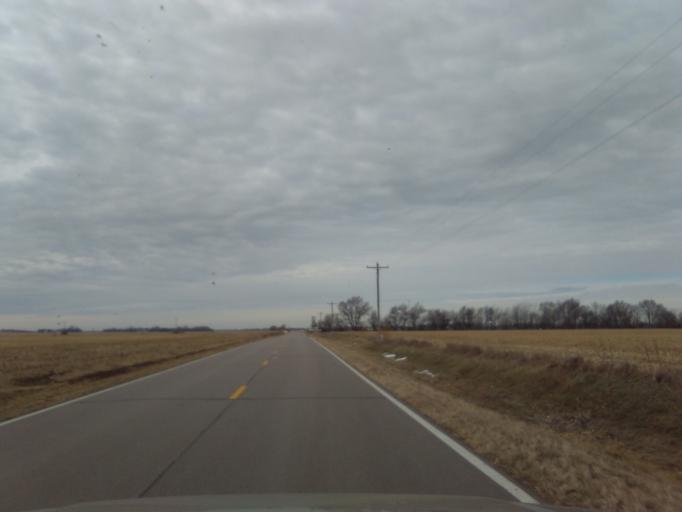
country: US
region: Nebraska
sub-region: Hall County
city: Wood River
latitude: 40.7711
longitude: -98.4310
